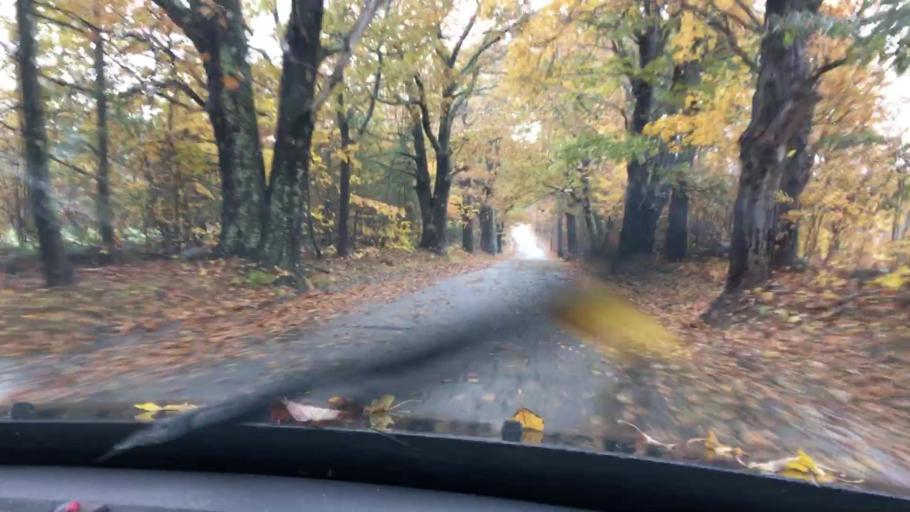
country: US
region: New Hampshire
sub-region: Belknap County
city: Meredith
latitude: 43.6987
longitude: -71.5101
